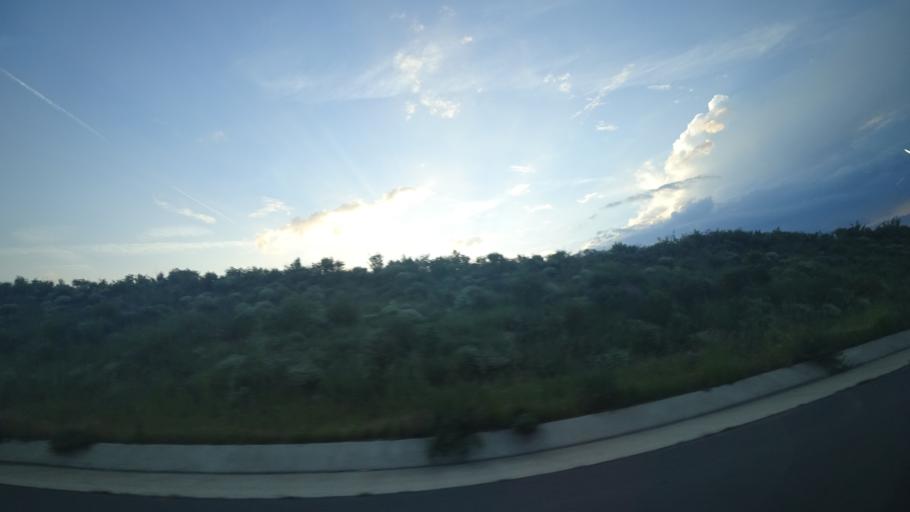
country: FR
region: Languedoc-Roussillon
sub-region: Departement de l'Herault
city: Tourbes
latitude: 43.4338
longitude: 3.3921
